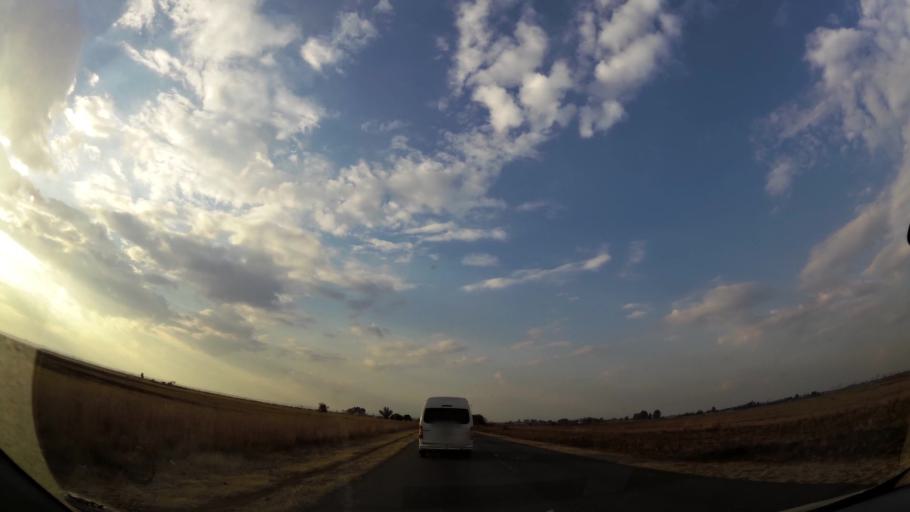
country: ZA
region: Gauteng
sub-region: Sedibeng District Municipality
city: Vanderbijlpark
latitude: -26.6265
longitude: 27.8103
